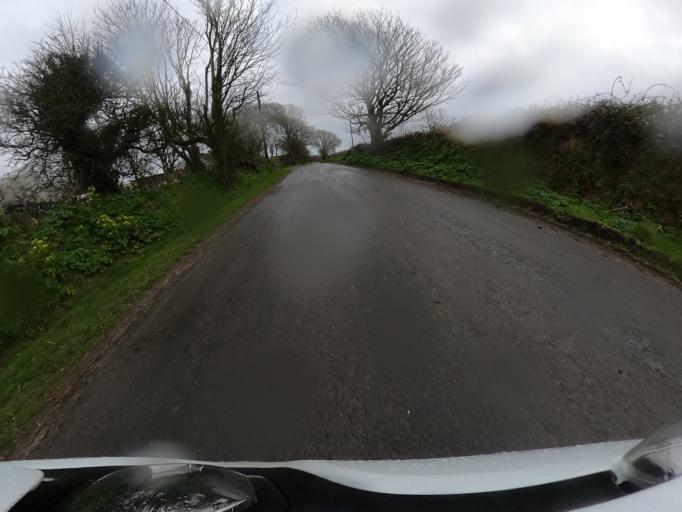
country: IM
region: Ramsey
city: Ramsey
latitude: 54.3691
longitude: -4.4576
